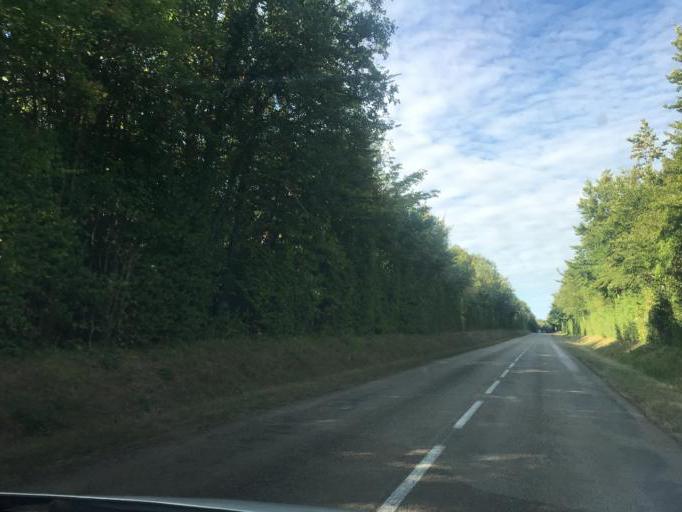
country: FR
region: Bourgogne
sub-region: Departement de l'Yonne
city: Fontenailles
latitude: 47.5724
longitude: 3.4543
